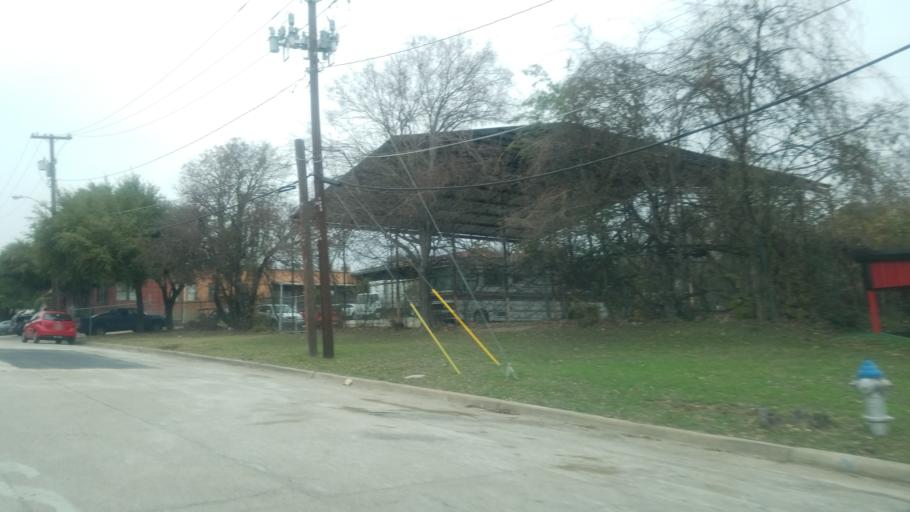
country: US
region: Texas
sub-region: Dallas County
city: Dallas
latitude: 32.8105
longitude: -96.8294
